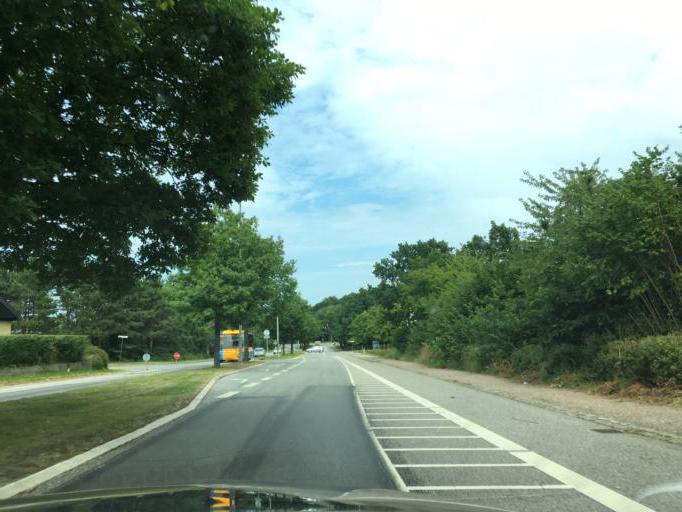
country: DK
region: Capital Region
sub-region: Fredensborg Kommune
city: Kokkedal
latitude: 55.8994
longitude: 12.4981
